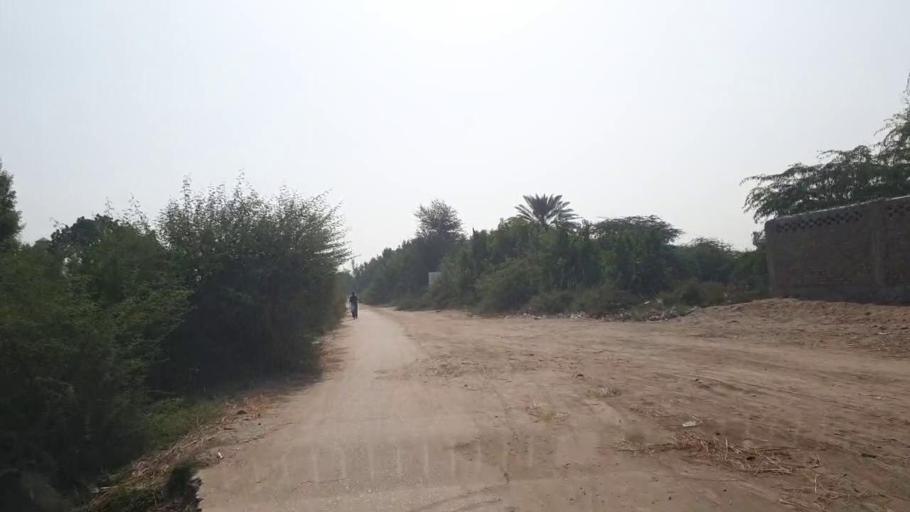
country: PK
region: Sindh
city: Badin
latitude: 24.6539
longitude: 68.8428
